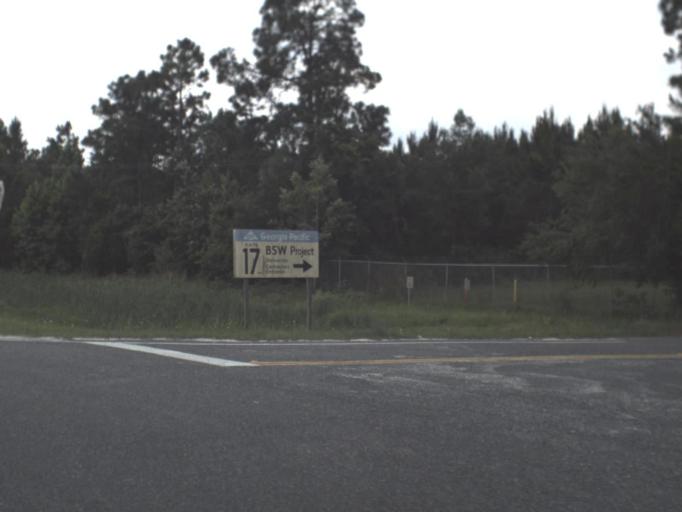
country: US
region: Florida
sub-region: Putnam County
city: Palatka
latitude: 29.6883
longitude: -81.6627
